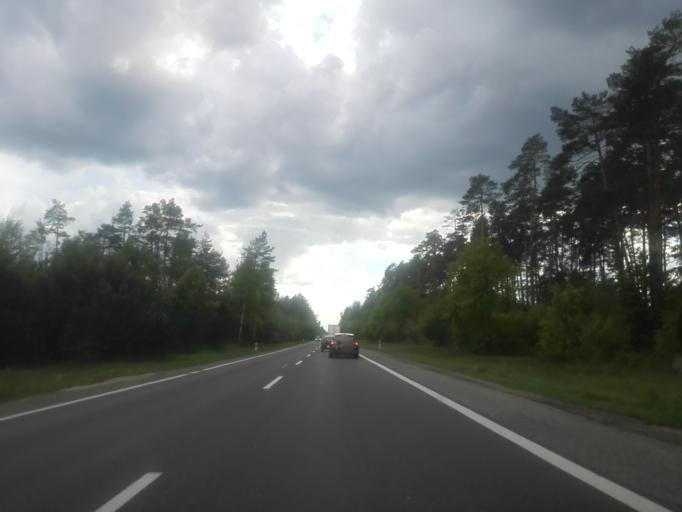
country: PL
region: Masovian Voivodeship
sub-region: Powiat ostrowski
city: Ostrow Mazowiecka
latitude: 52.7720
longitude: 21.8299
